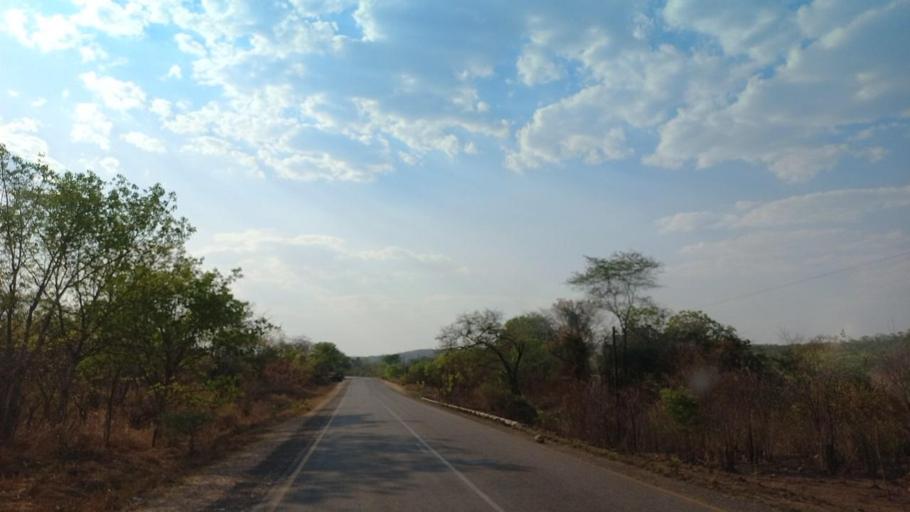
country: ZM
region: Lusaka
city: Luangwa
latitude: -14.9689
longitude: 30.0229
